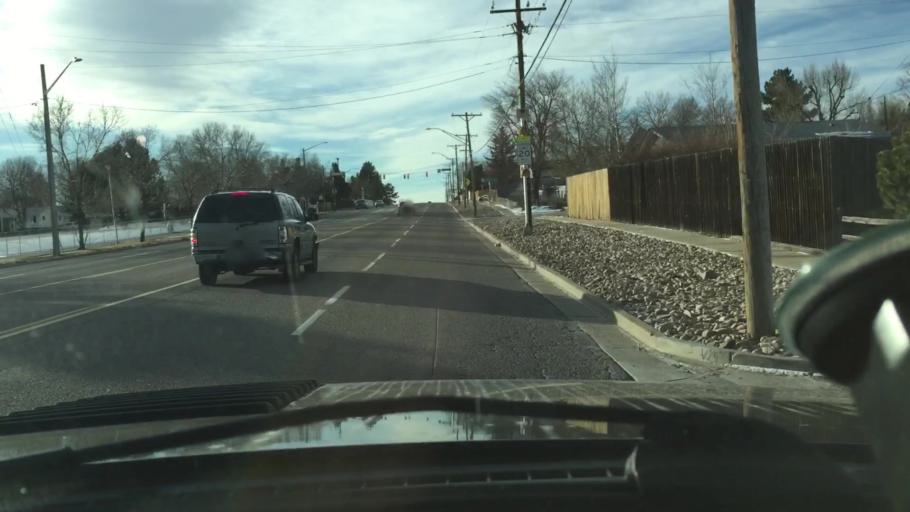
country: US
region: Colorado
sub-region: Adams County
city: Northglenn
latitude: 39.8799
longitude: -104.9967
